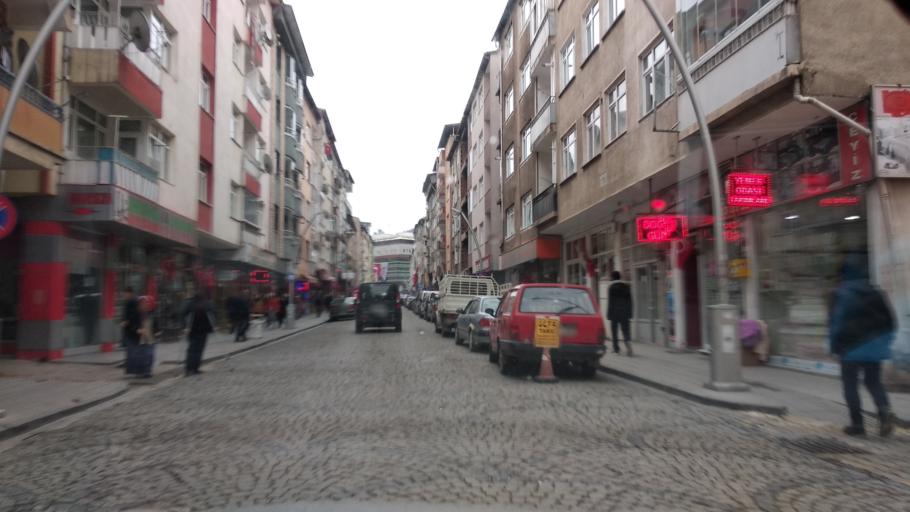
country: TR
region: Gumushane
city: Gumushkhane
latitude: 40.4603
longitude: 39.4757
